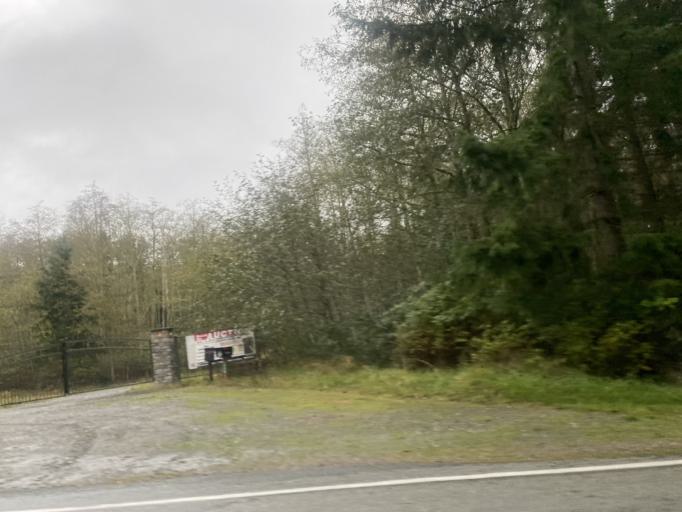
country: US
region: Washington
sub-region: Island County
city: Freeland
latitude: 48.0864
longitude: -122.4981
